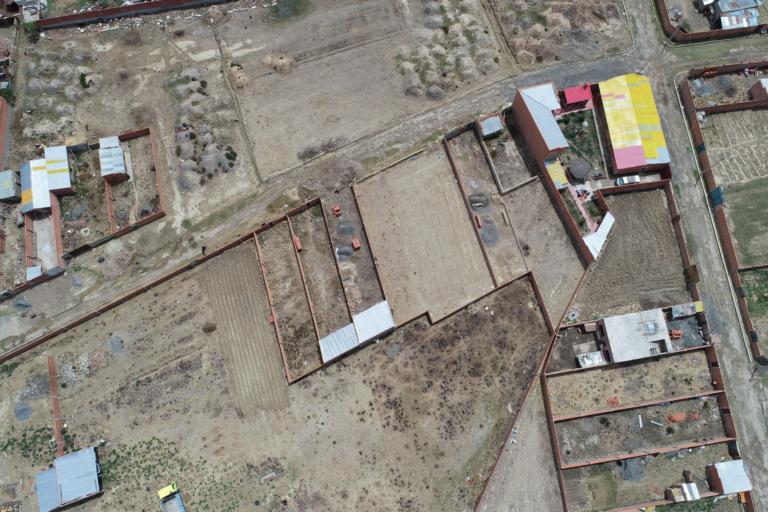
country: BO
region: La Paz
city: Achacachi
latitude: -16.0544
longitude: -68.6819
